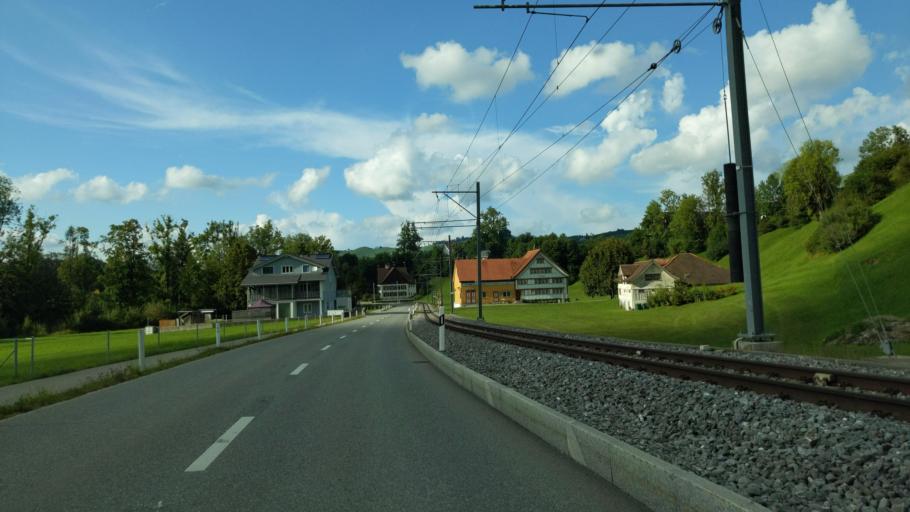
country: CH
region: Appenzell Innerrhoden
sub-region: Appenzell Inner Rhodes
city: Appenzell
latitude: 47.3155
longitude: 9.4342
